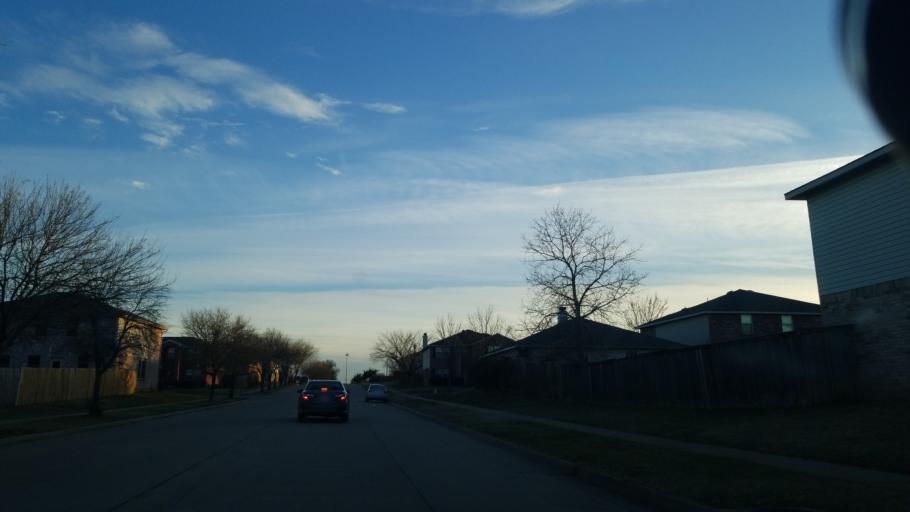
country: US
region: Texas
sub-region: Denton County
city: Corinth
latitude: 33.1576
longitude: -97.0973
